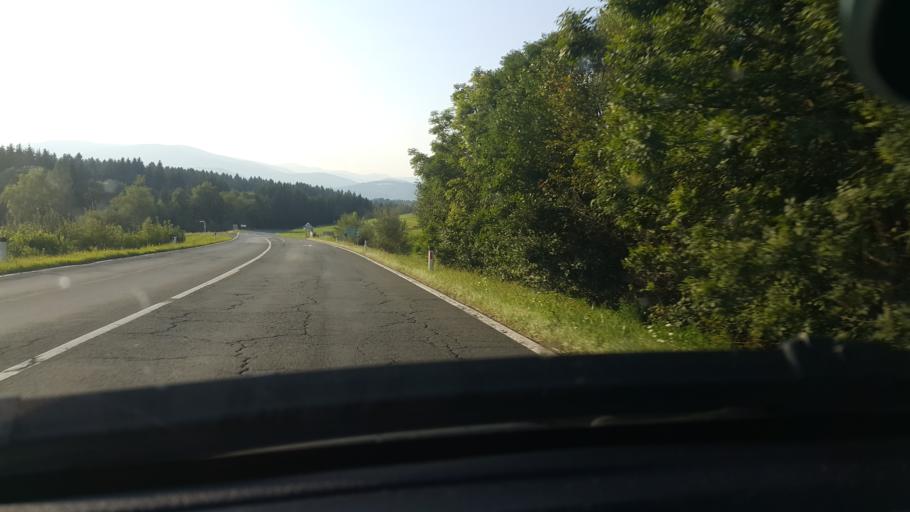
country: AT
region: Carinthia
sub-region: Politischer Bezirk Feldkirchen
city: Feldkirchen in Karnten
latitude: 46.6984
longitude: 14.1220
